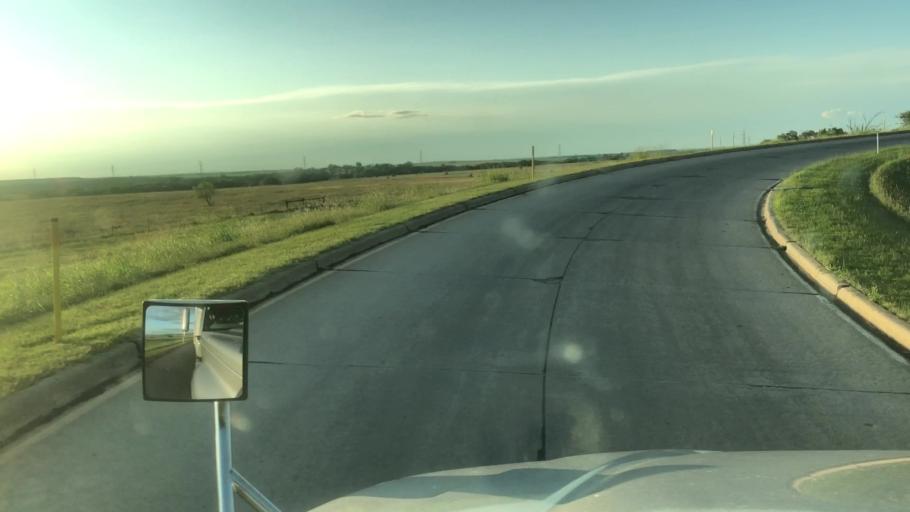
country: US
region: Oklahoma
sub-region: Noble County
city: Perry
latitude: 36.3843
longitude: -97.0692
